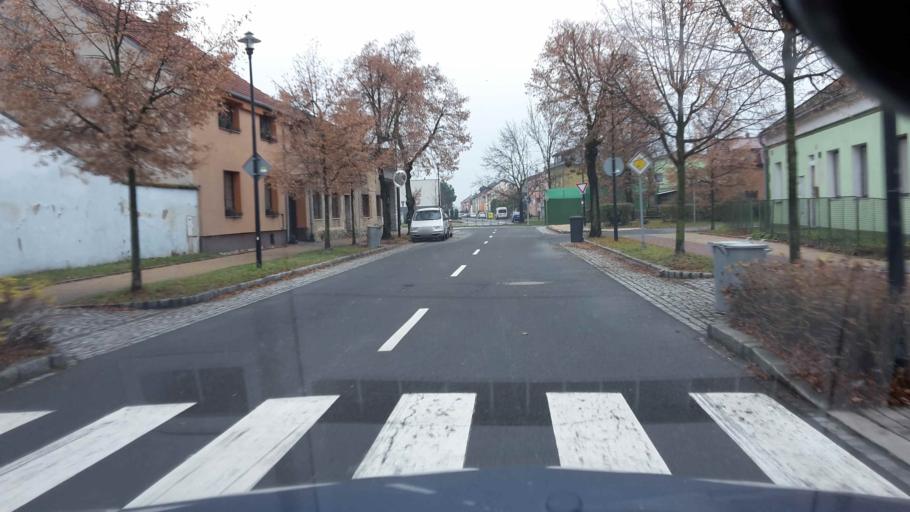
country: CZ
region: Olomoucky
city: Grygov
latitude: 49.5705
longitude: 17.2964
